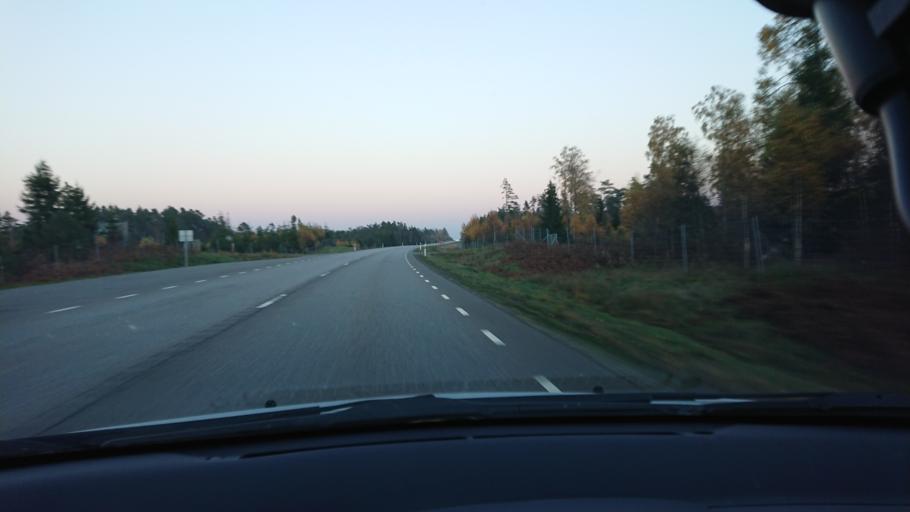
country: SE
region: Kronoberg
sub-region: Markaryds Kommun
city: Stromsnasbruk
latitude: 56.7516
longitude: 13.5089
